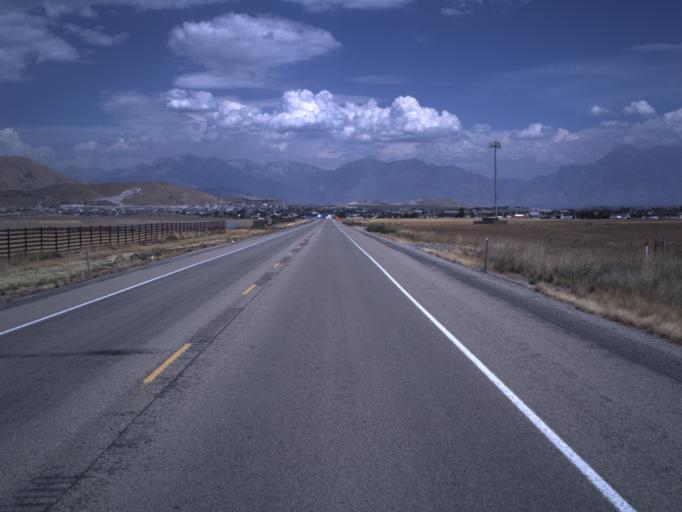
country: US
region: Utah
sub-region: Utah County
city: Eagle Mountain
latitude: 40.3684
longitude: -112.0307
